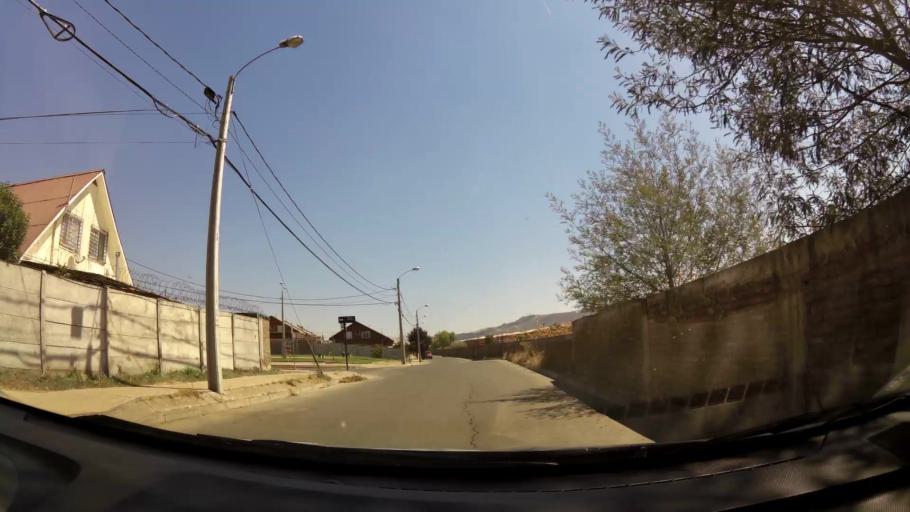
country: CL
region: Maule
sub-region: Provincia de Talca
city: Talca
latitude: -35.4007
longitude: -71.6449
